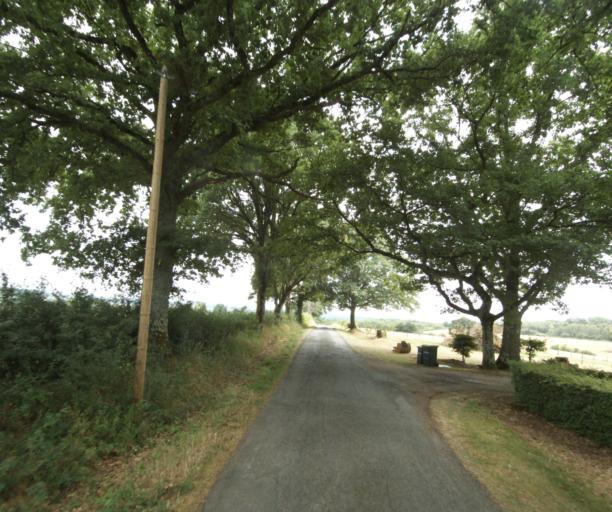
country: FR
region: Bourgogne
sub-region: Departement de Saone-et-Loire
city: Gueugnon
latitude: 46.5848
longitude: 4.0372
